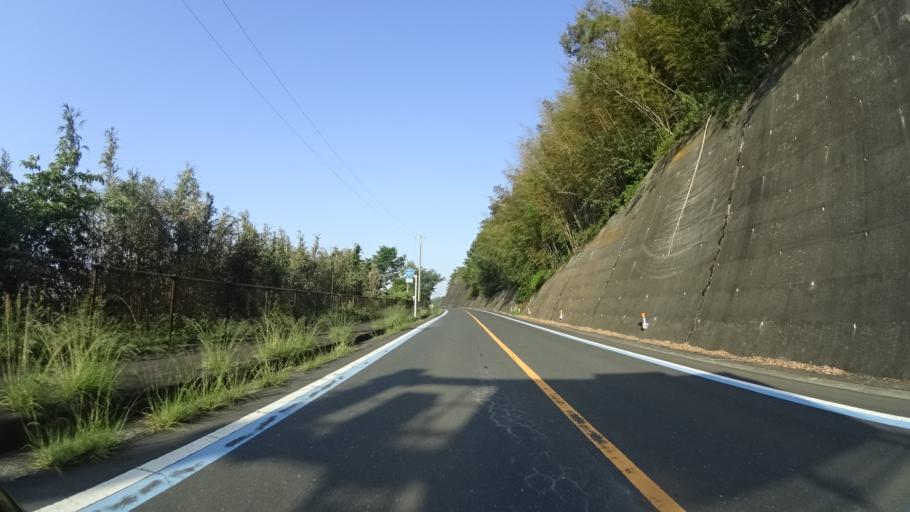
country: JP
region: Ehime
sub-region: Nishiuwa-gun
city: Ikata-cho
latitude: 33.4926
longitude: 132.3570
